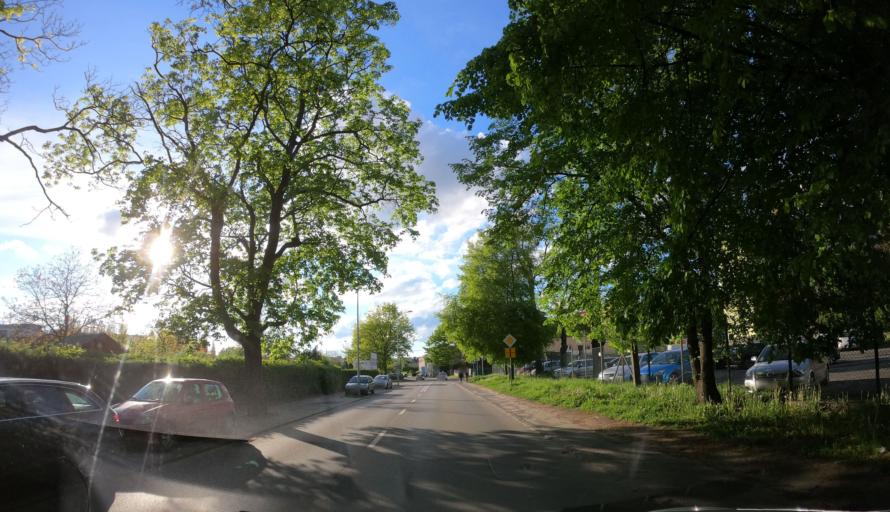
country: PL
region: West Pomeranian Voivodeship
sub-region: Szczecin
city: Szczecin
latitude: 53.4130
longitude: 14.5401
